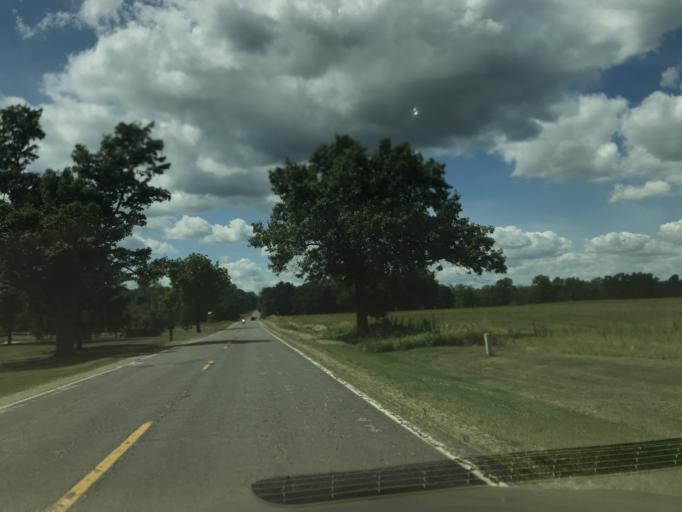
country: US
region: Michigan
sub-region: Ingham County
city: Leslie
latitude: 42.4509
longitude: -84.5371
